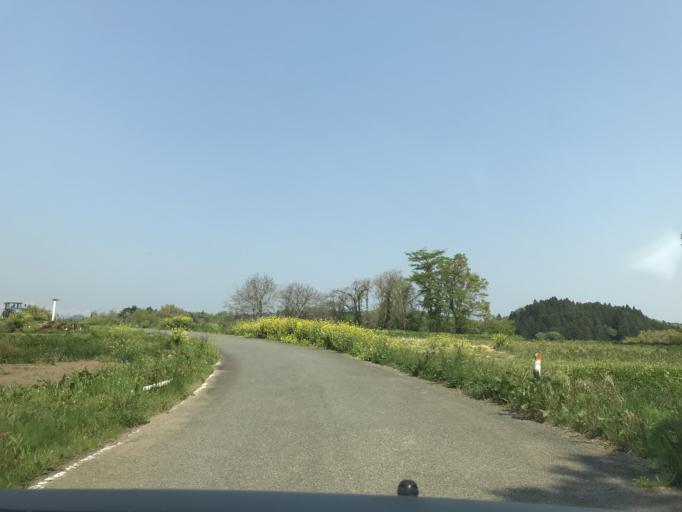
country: JP
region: Iwate
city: Ichinoseki
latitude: 38.8583
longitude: 141.0595
